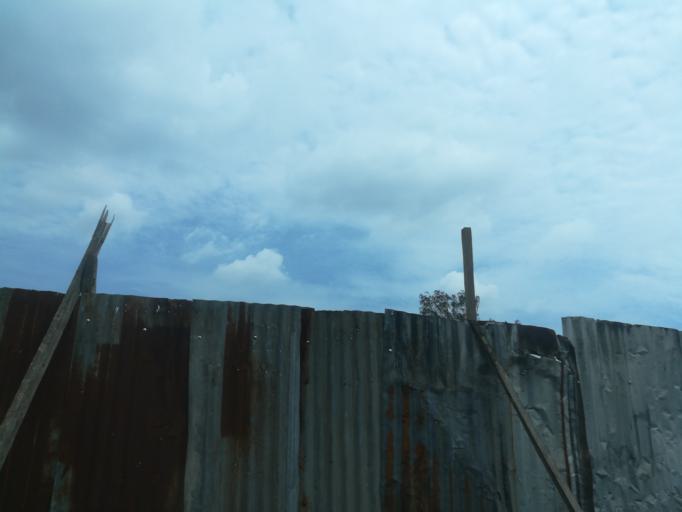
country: NG
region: Lagos
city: Ojota
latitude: 6.5748
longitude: 3.3681
